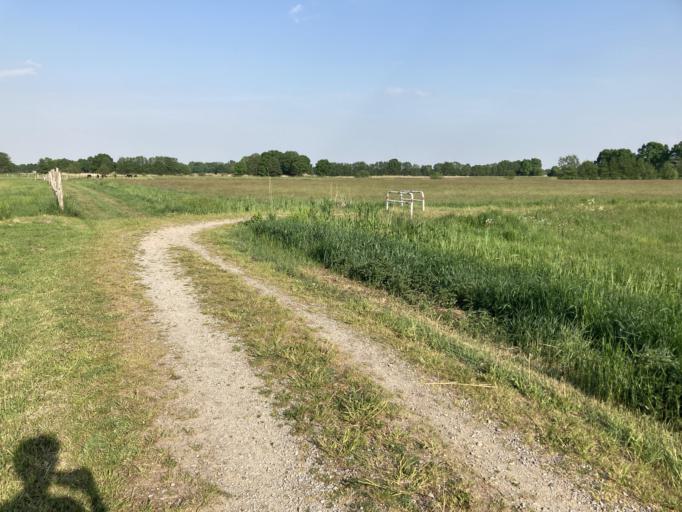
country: DE
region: Lower Saxony
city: Brietlingen
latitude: 53.3450
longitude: 10.4437
